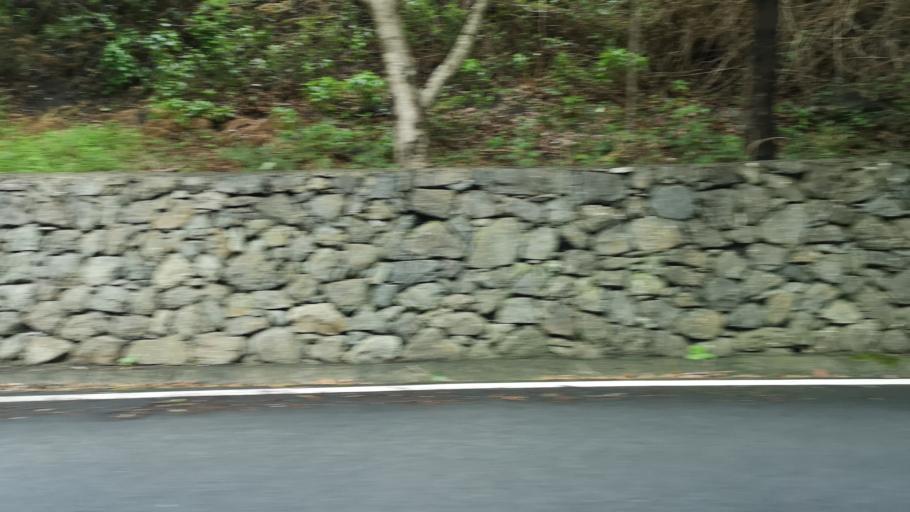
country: ES
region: Canary Islands
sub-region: Provincia de Santa Cruz de Tenerife
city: Hermigua
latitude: 28.1290
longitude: -17.2058
